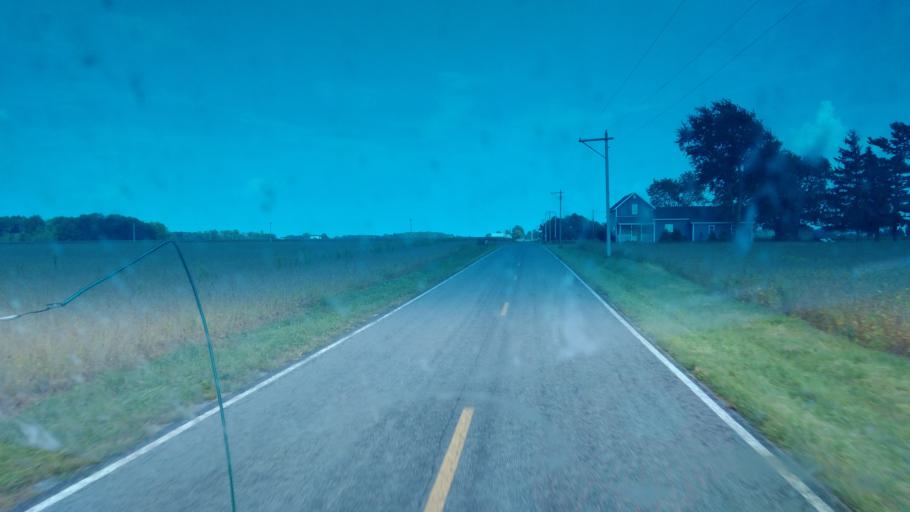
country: US
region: Ohio
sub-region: Hardin County
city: Forest
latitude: 40.9050
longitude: -83.5040
